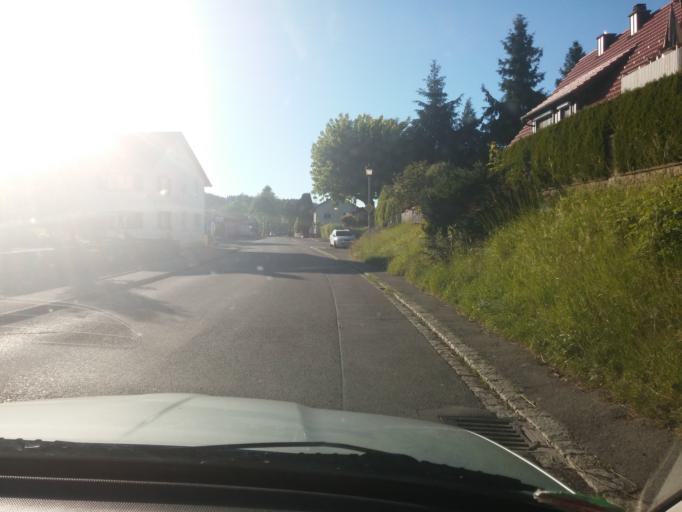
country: DE
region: Bavaria
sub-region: Swabia
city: Woringen
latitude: 47.8784
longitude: 10.2194
